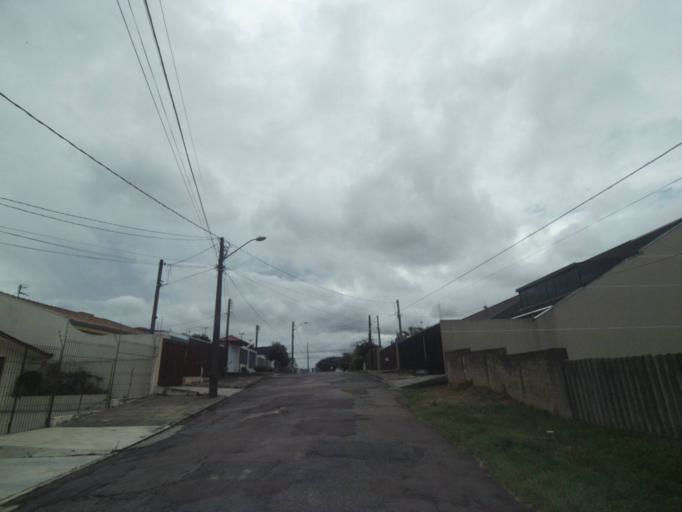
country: BR
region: Parana
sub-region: Curitiba
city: Curitiba
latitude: -25.4764
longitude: -49.2755
